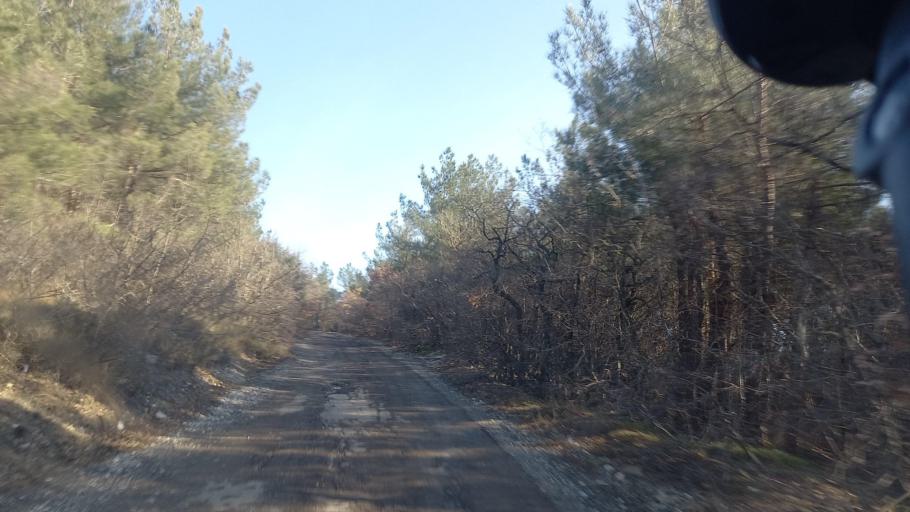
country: RU
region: Krasnodarskiy
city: Kabardinka
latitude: 44.6294
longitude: 37.9170
